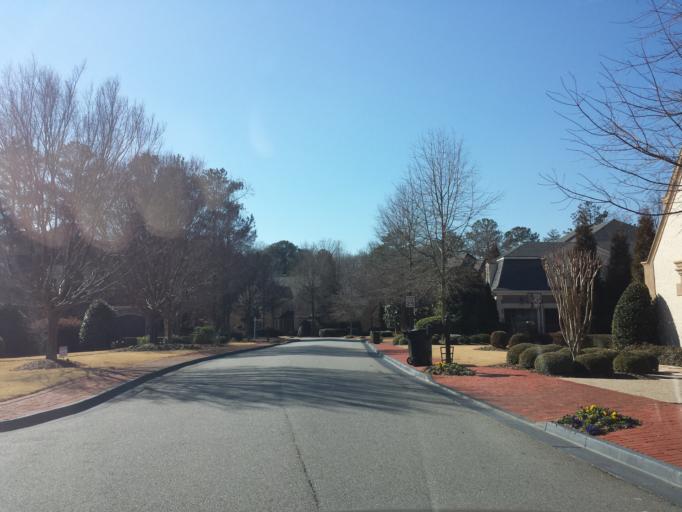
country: US
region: Georgia
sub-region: Cobb County
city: Vinings
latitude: 33.9167
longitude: -84.4544
